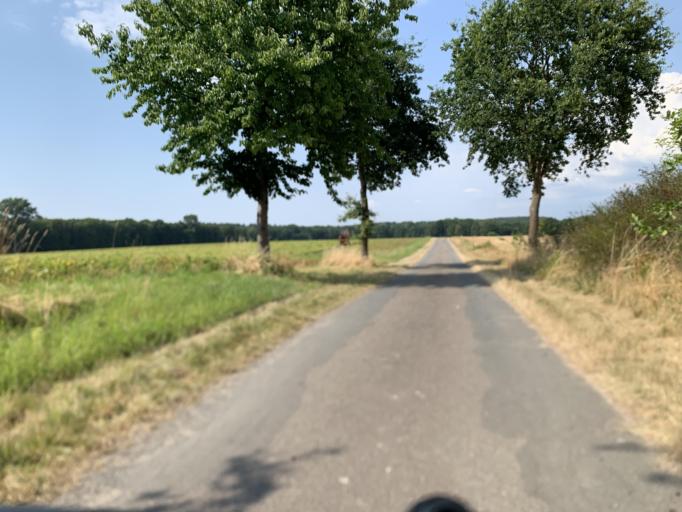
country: DE
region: Lower Saxony
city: Neetze
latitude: 53.2377
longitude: 10.6324
